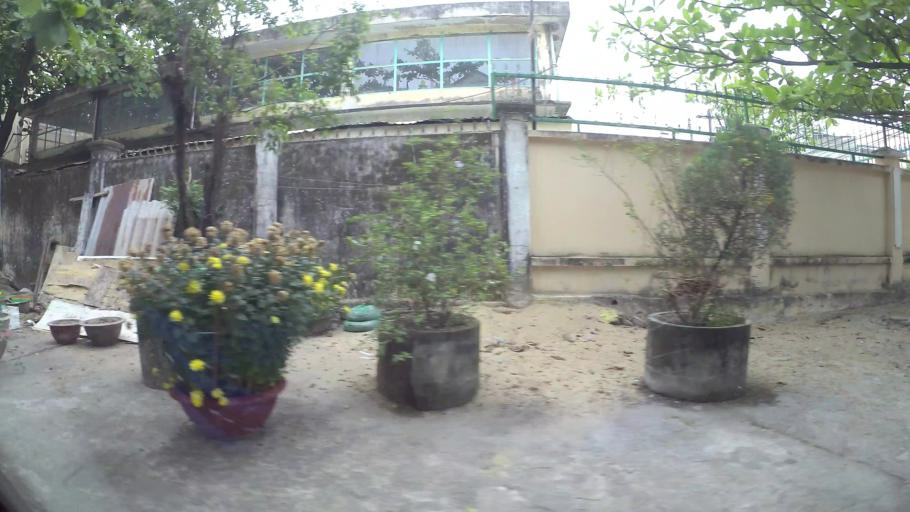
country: VN
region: Da Nang
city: Thanh Khe
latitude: 16.0631
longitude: 108.1912
